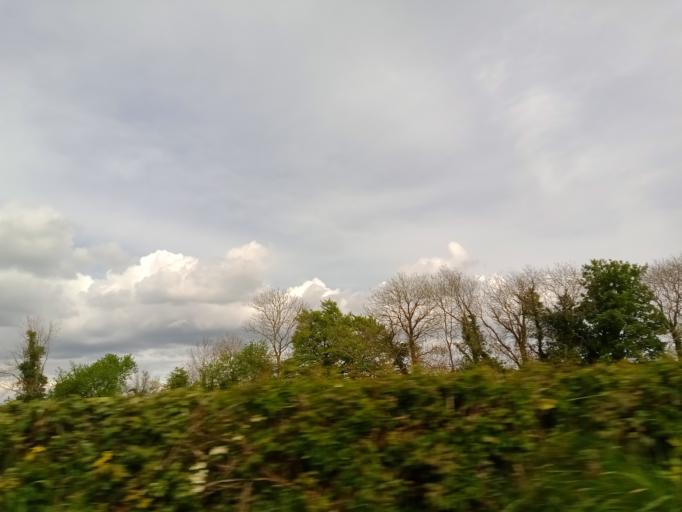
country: IE
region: Munster
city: Thurles
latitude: 52.6150
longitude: -7.7882
